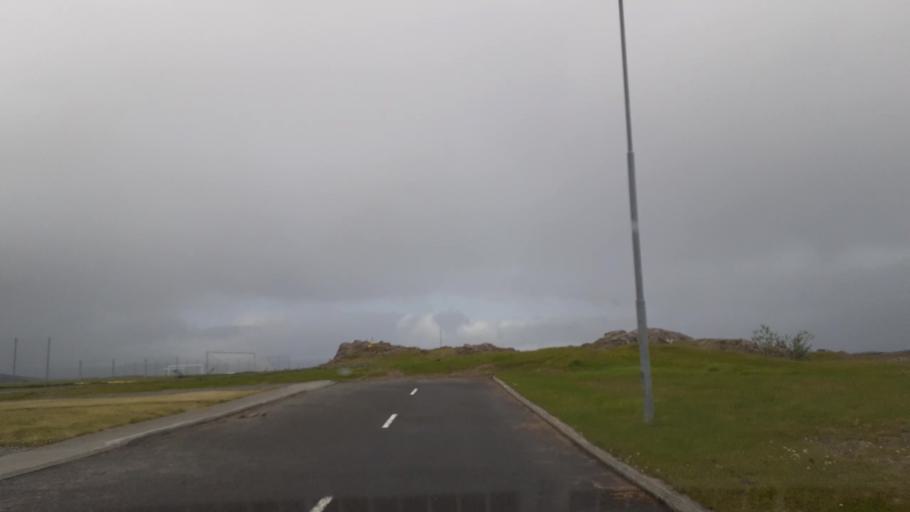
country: IS
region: East
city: Egilsstadir
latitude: 65.7542
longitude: -14.8355
